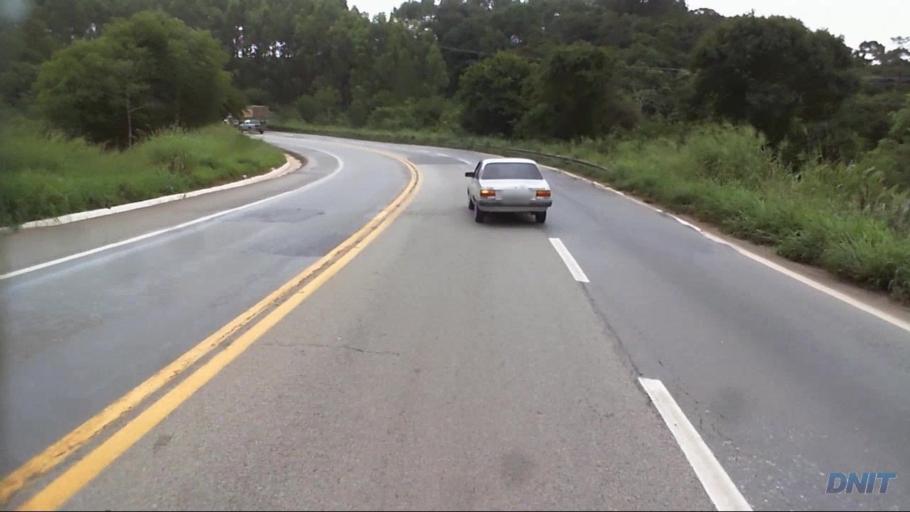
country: BR
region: Minas Gerais
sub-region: Caete
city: Caete
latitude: -19.7517
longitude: -43.5353
